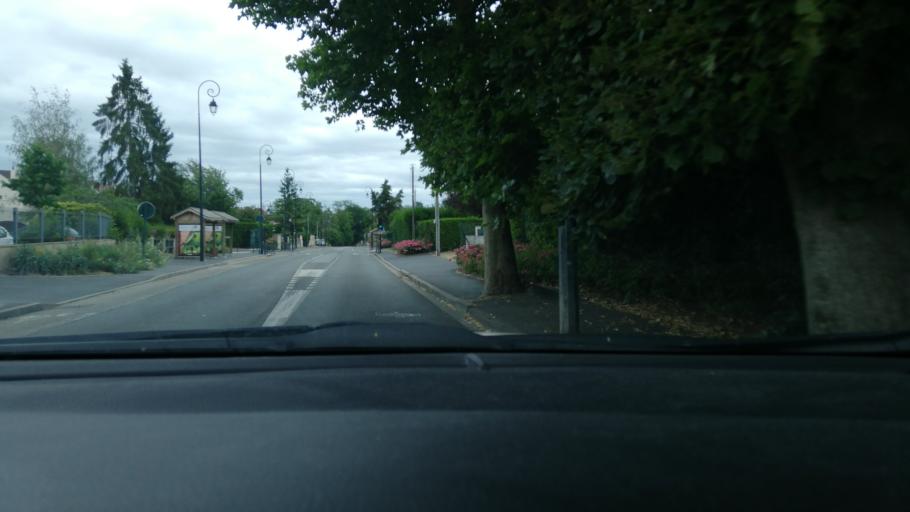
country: FR
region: Ile-de-France
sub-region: Departement du Val-d'Oise
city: Auvers-sur-Oise
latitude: 49.0757
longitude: 2.1619
